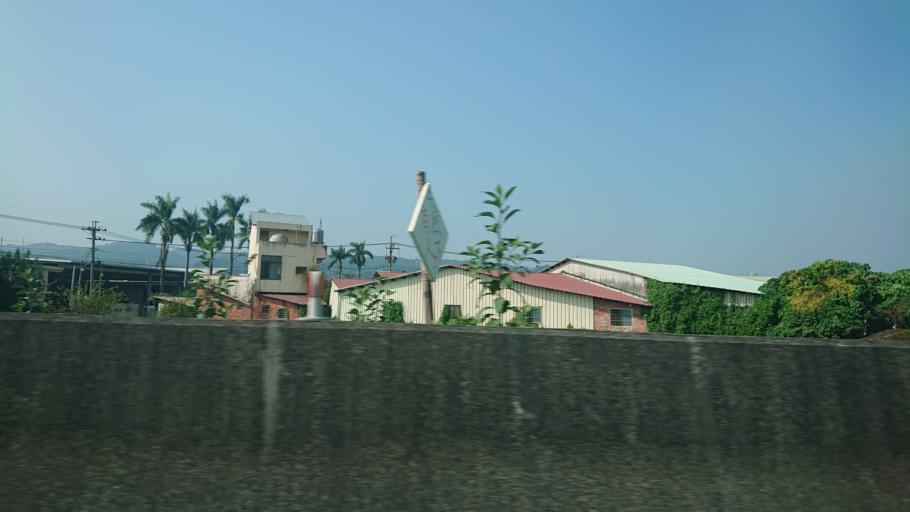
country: TW
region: Taiwan
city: Lugu
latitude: 23.7651
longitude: 120.6598
